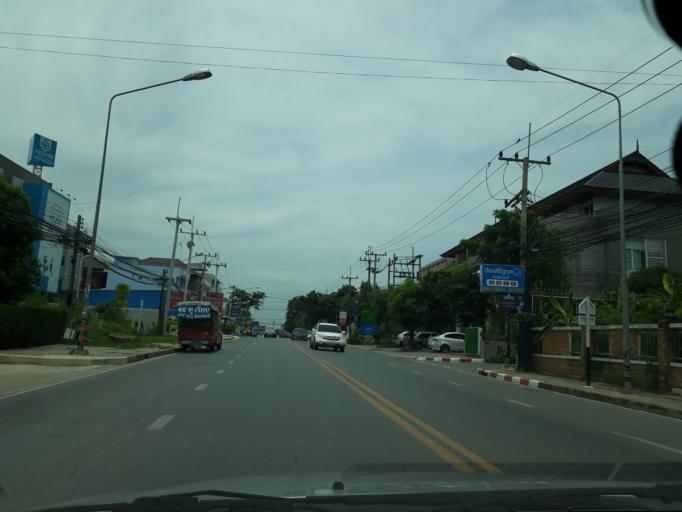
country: TH
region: Khon Kaen
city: Khon Kaen
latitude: 16.4345
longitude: 102.8582
